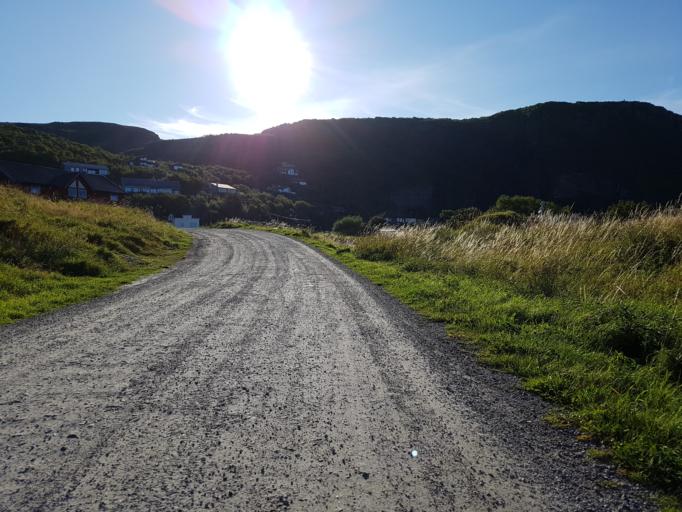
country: NO
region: Sor-Trondelag
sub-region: Afjord
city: A i Afjord
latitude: 64.0545
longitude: 9.9517
